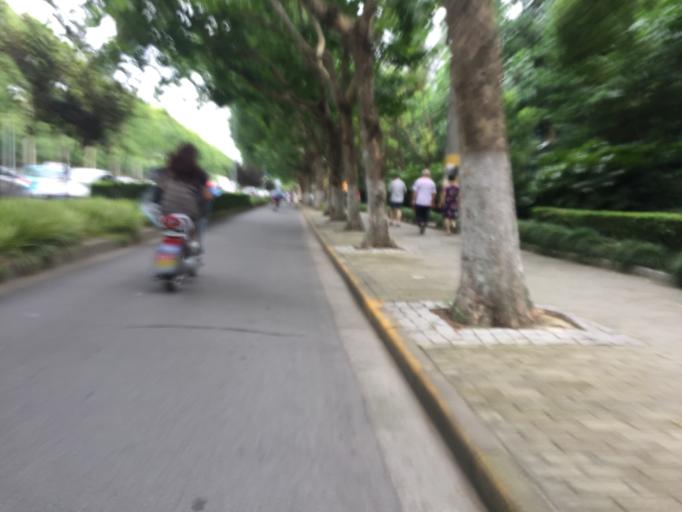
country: CN
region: Shanghai Shi
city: Huamu
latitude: 31.1839
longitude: 121.5370
